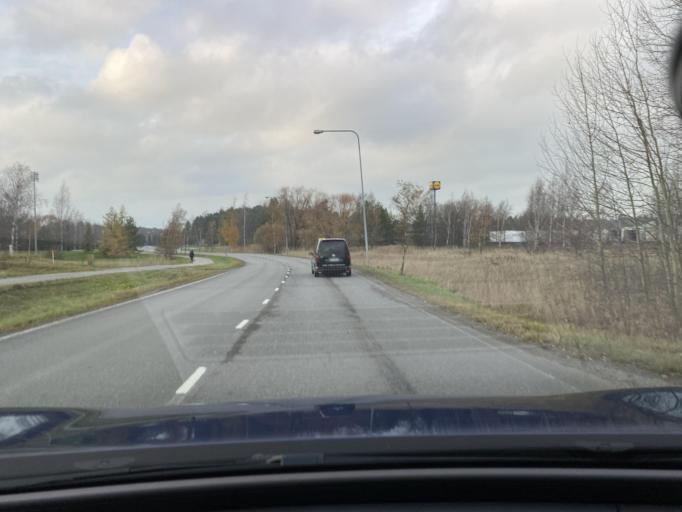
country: FI
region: Varsinais-Suomi
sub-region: Turku
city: Naantali
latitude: 60.4741
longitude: 22.0515
